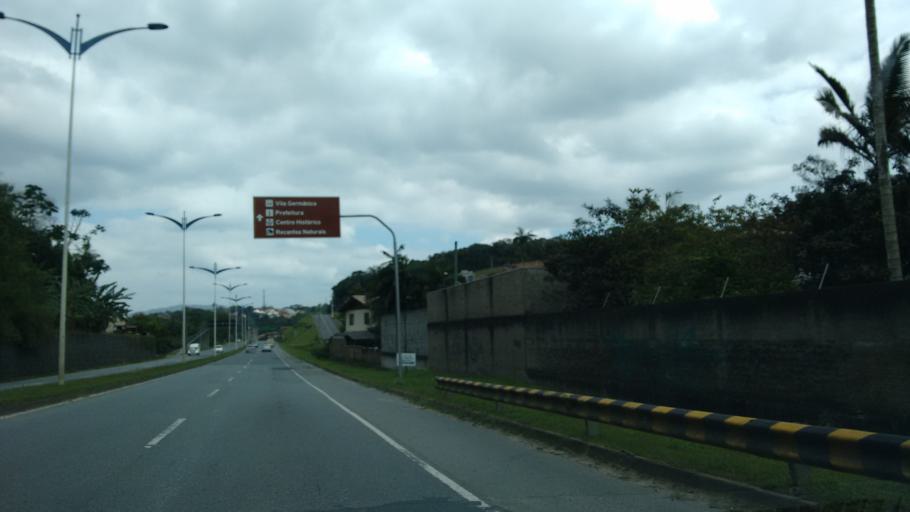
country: BR
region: Santa Catarina
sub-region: Blumenau
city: Blumenau
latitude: -26.8610
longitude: -49.0713
